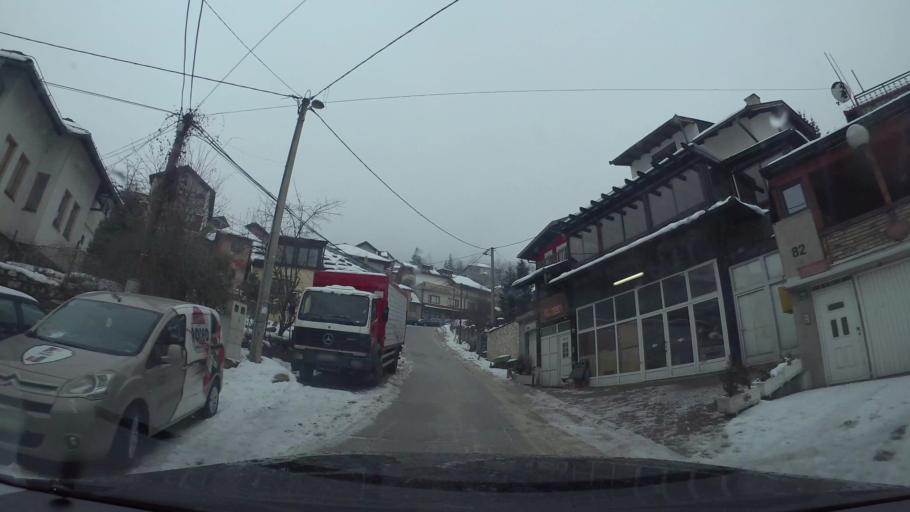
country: BA
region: Federation of Bosnia and Herzegovina
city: Kobilja Glava
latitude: 43.8517
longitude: 18.4310
